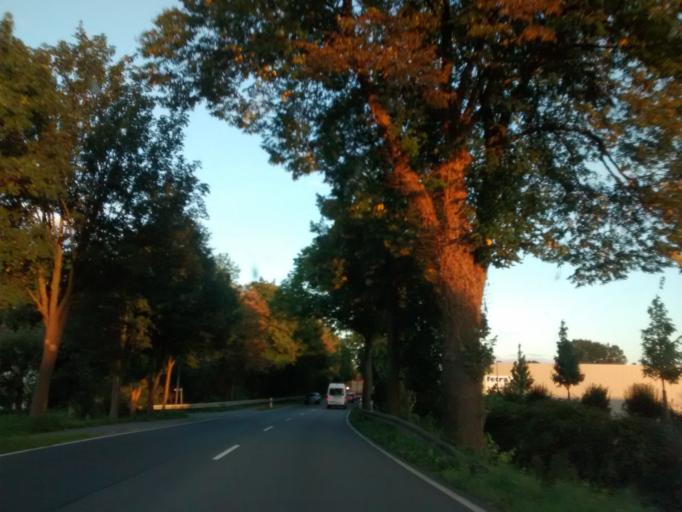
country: DE
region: North Rhine-Westphalia
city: Borgholzhausen
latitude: 52.0845
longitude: 8.2760
